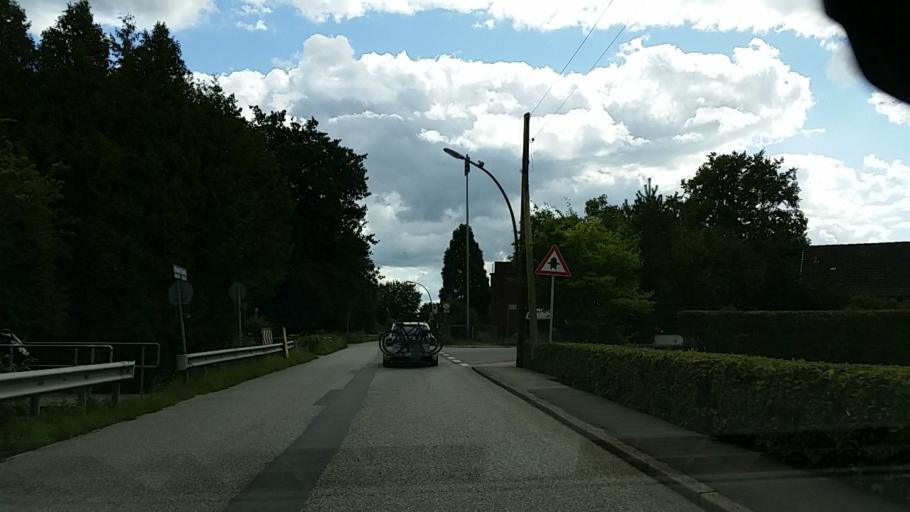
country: DE
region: Schleswig-Holstein
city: Bornsen
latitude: 53.4560
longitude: 10.2831
